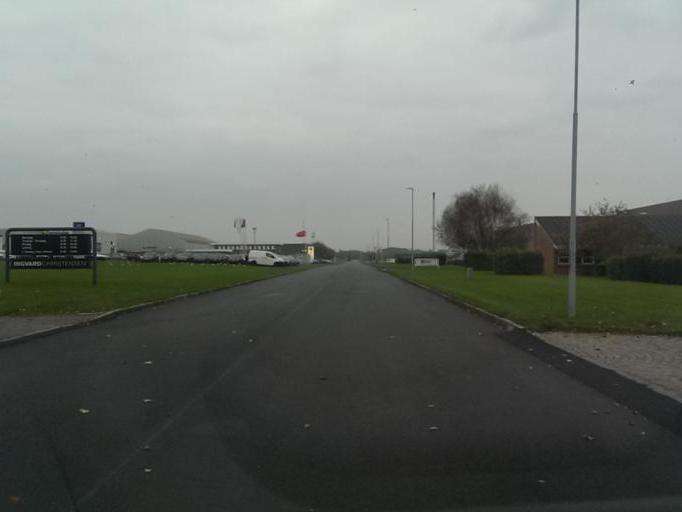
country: DK
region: South Denmark
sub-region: Esbjerg Kommune
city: Esbjerg
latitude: 55.5067
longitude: 8.4685
